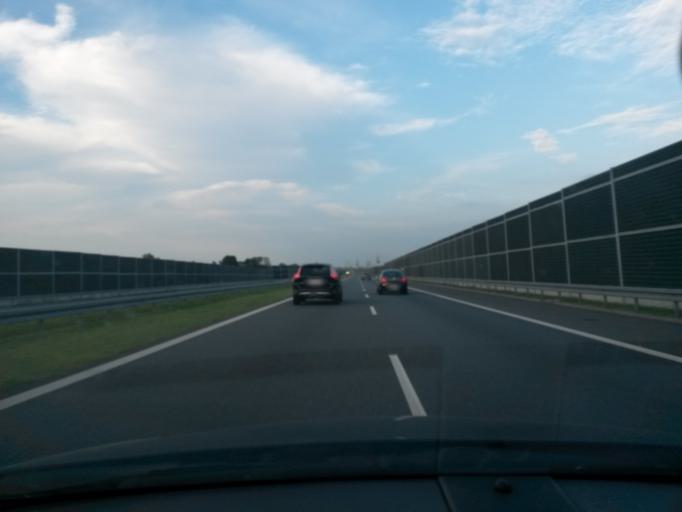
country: PL
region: Masovian Voivodeship
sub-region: Powiat zyrardowski
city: Zyrardow
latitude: 52.1056
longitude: 20.4432
